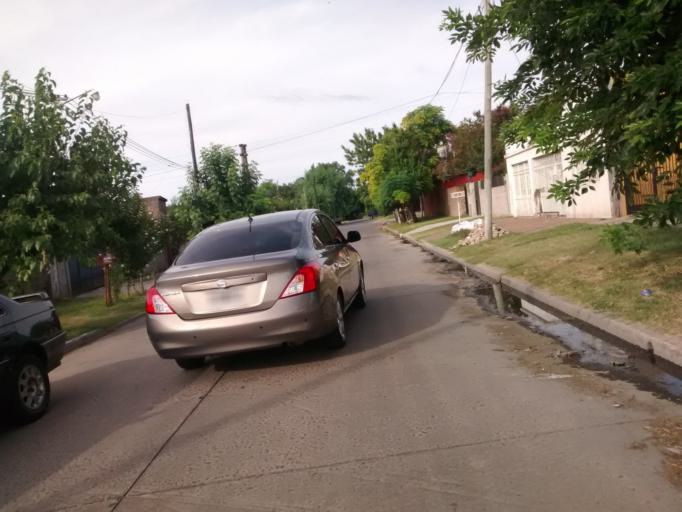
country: AR
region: Buenos Aires
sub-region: Partido de La Plata
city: La Plata
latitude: -34.8534
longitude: -58.0723
